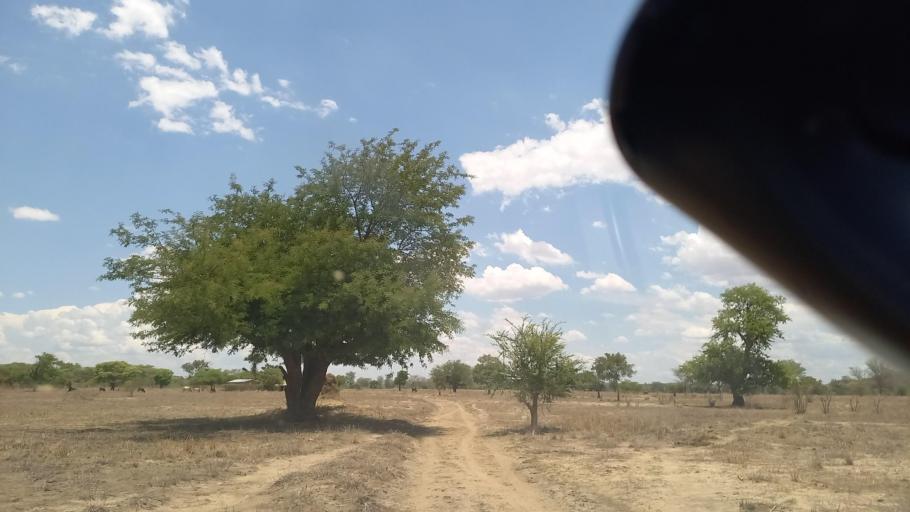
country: ZM
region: Southern
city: Mazabuka
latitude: -16.1262
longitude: 27.7788
